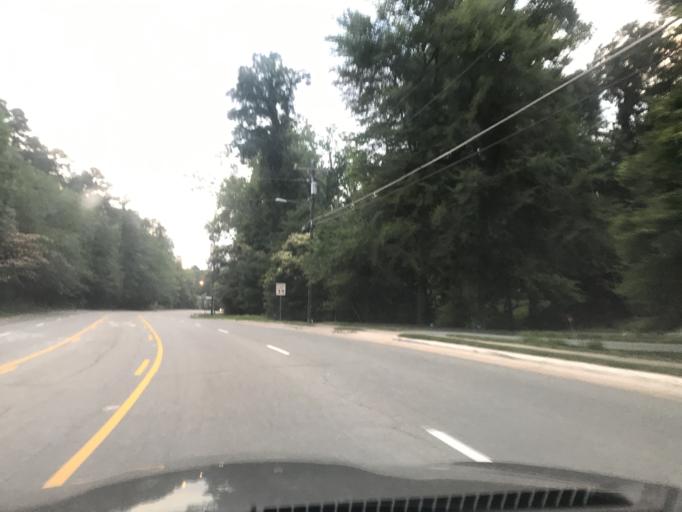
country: US
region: North Carolina
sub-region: Orange County
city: Chapel Hill
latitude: 35.9213
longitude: -79.0387
